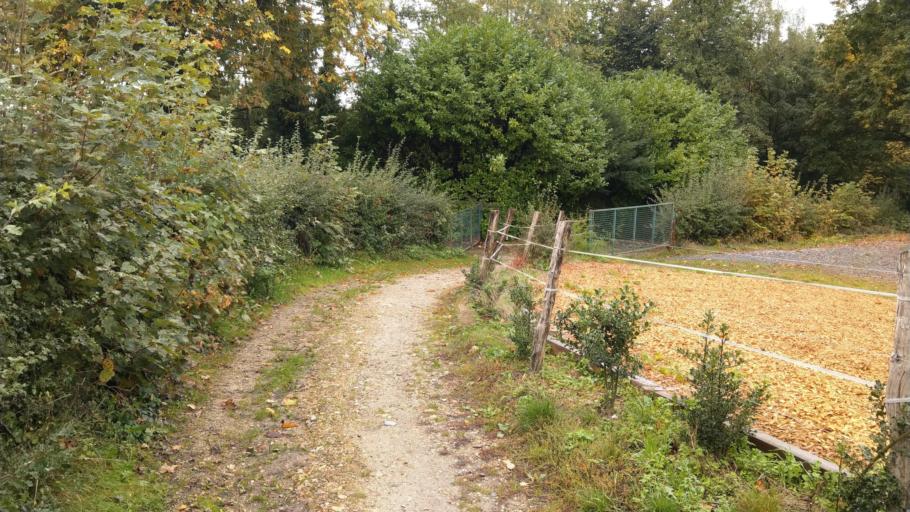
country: NL
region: Limburg
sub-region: Gemeente Vaals
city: Vaals
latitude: 50.7526
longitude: 6.0039
